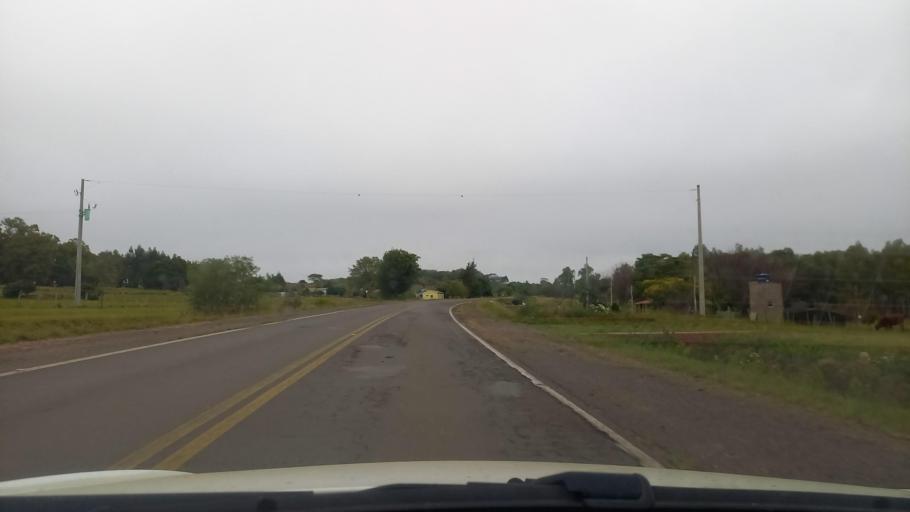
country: BR
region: Rio Grande do Sul
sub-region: Cacequi
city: Cacequi
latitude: -30.1216
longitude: -54.6398
